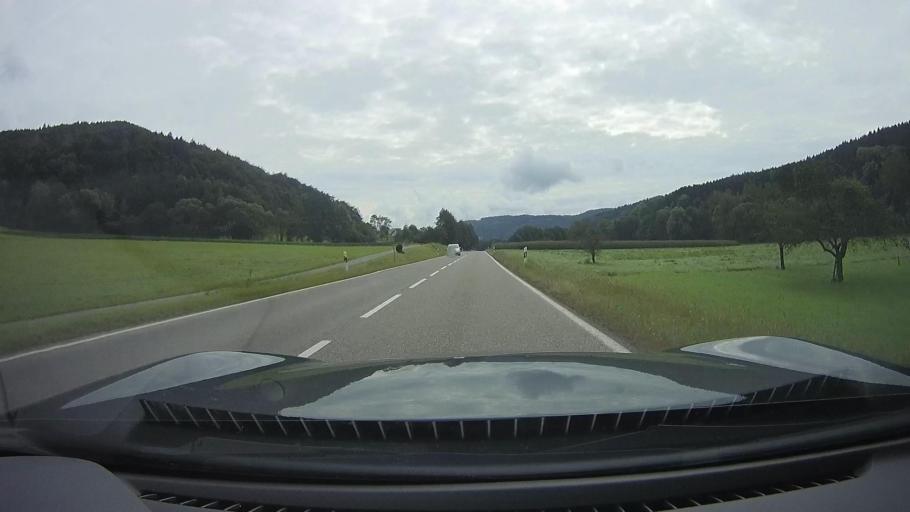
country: DE
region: Baden-Wuerttemberg
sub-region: Regierungsbezirk Stuttgart
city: Sulzbach an der Murr
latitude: 49.0158
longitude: 9.4712
